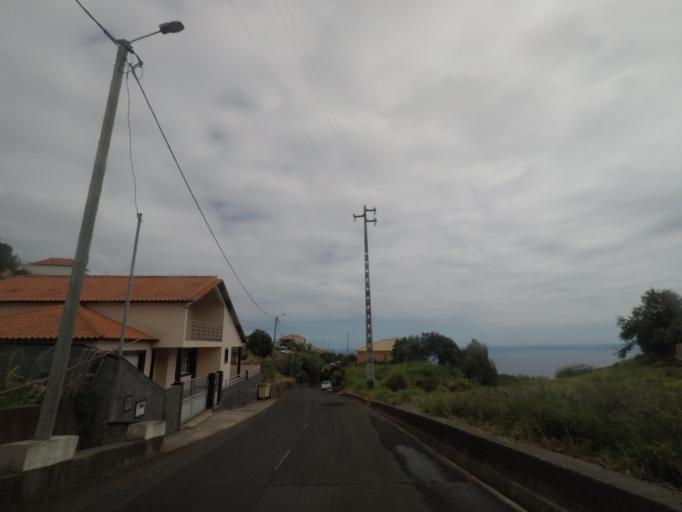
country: PT
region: Madeira
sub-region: Calheta
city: Estreito da Calheta
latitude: 32.7337
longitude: -17.1740
